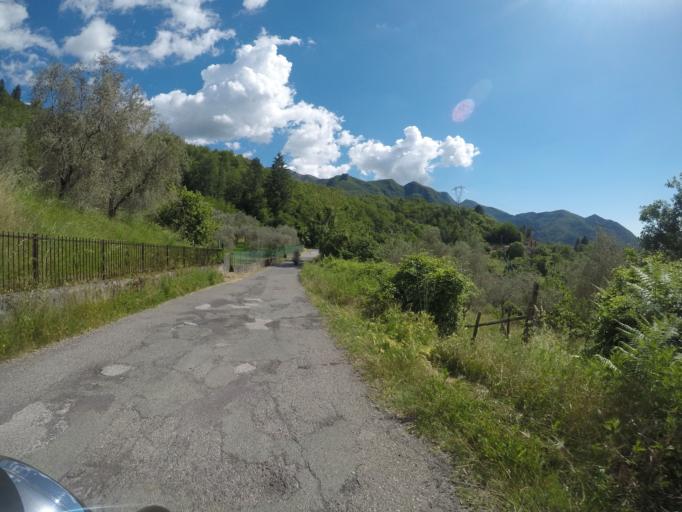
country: IT
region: Tuscany
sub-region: Provincia di Massa-Carrara
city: Casola in Lunigiana
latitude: 44.1782
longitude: 10.1521
